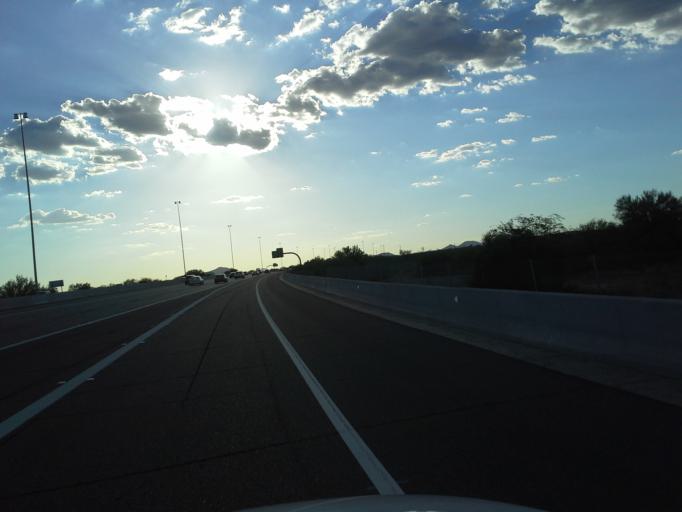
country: US
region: Arizona
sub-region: Maricopa County
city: Paradise Valley
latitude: 33.6629
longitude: -111.9469
